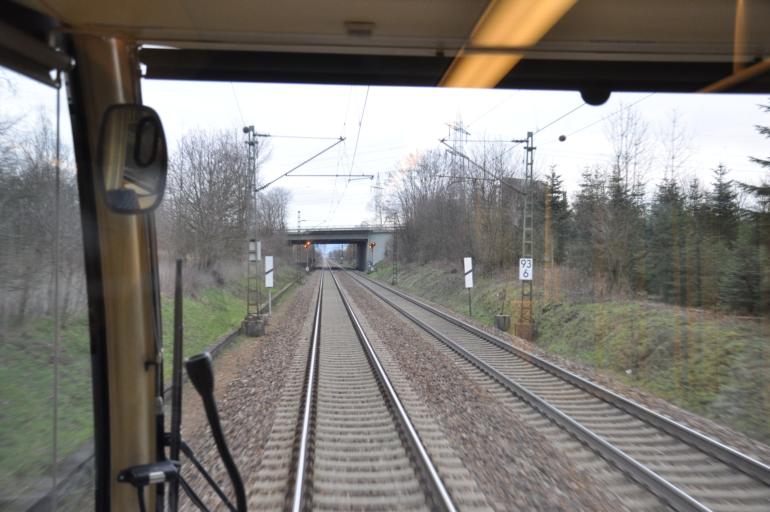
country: DE
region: Baden-Wuerttemberg
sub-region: Karlsruhe Region
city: Otigheim
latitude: 48.8707
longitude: 8.2508
